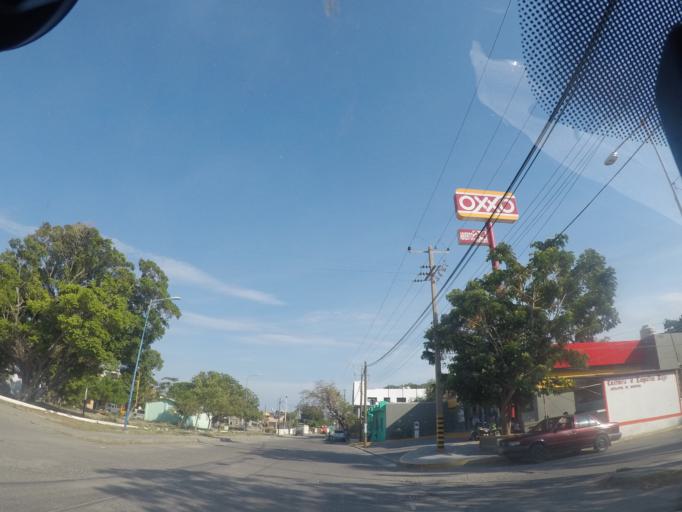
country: MX
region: Oaxaca
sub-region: Salina Cruz
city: Salina Cruz
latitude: 16.1787
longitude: -95.1984
